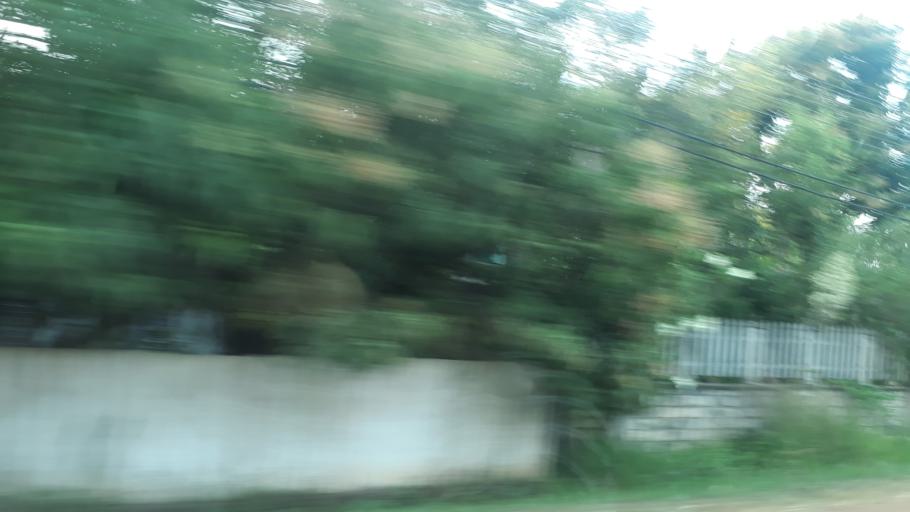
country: LK
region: North Central
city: Anuradhapura
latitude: 8.2961
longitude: 80.3754
